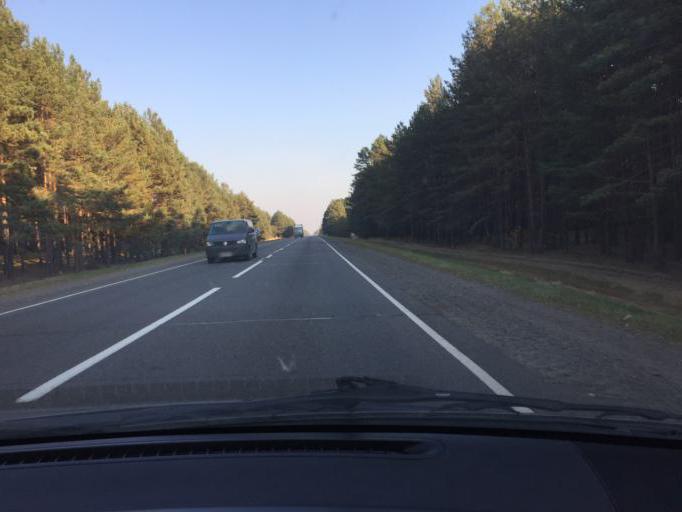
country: BY
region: Brest
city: Davyd-Haradok
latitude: 52.2472
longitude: 27.0965
